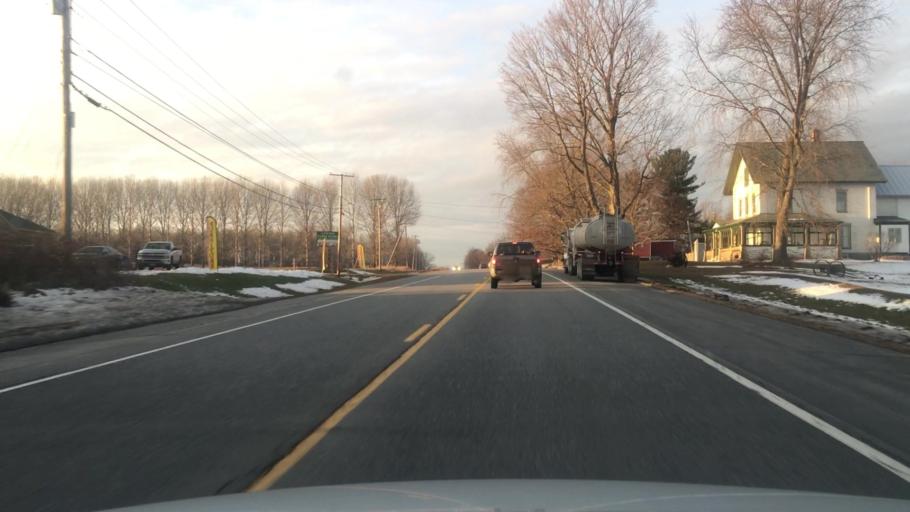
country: US
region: Maine
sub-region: Somerset County
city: Fairfield
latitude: 44.6332
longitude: -69.5956
